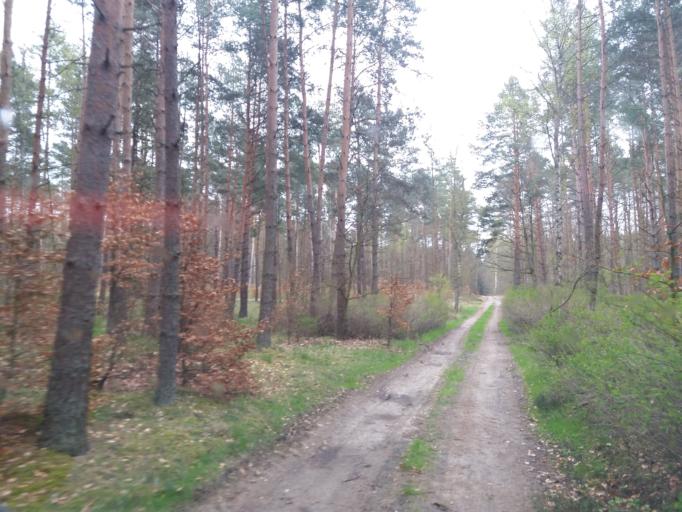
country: PL
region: West Pomeranian Voivodeship
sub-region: Powiat choszczenski
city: Drawno
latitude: 53.0983
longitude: 15.8349
